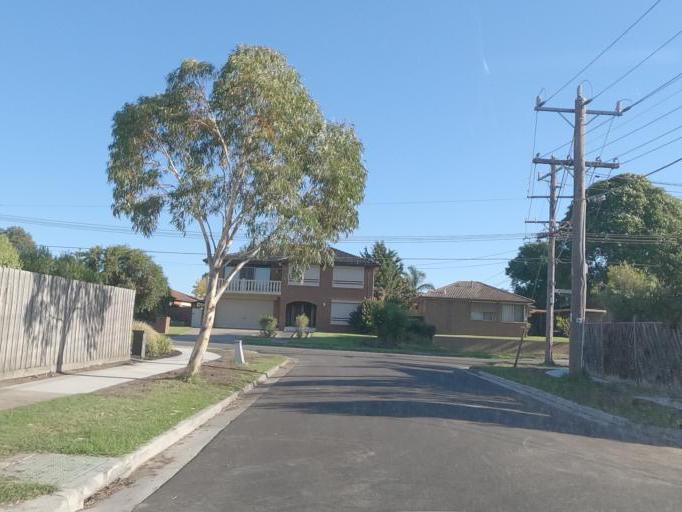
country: AU
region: Victoria
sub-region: Hume
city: Gladstone Park
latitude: -37.6863
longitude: 144.8915
